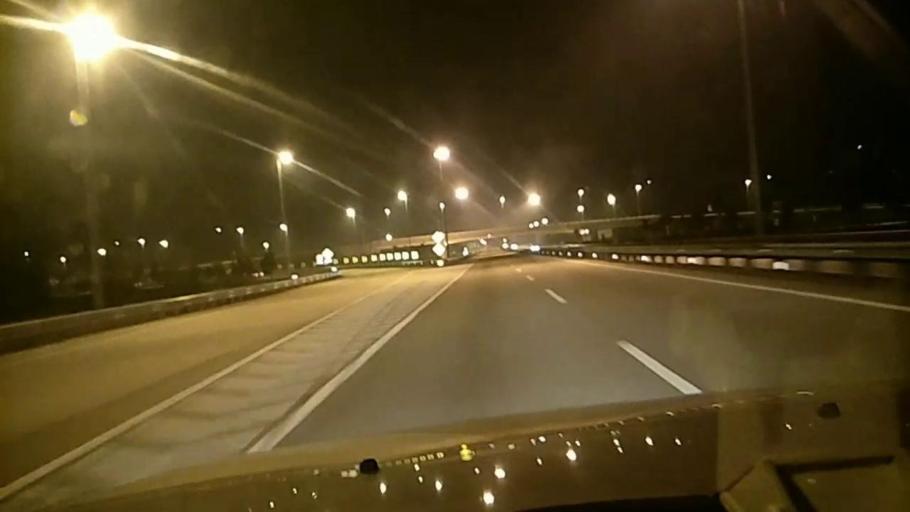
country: MY
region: Penang
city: Juru
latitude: 5.2486
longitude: 100.4716
